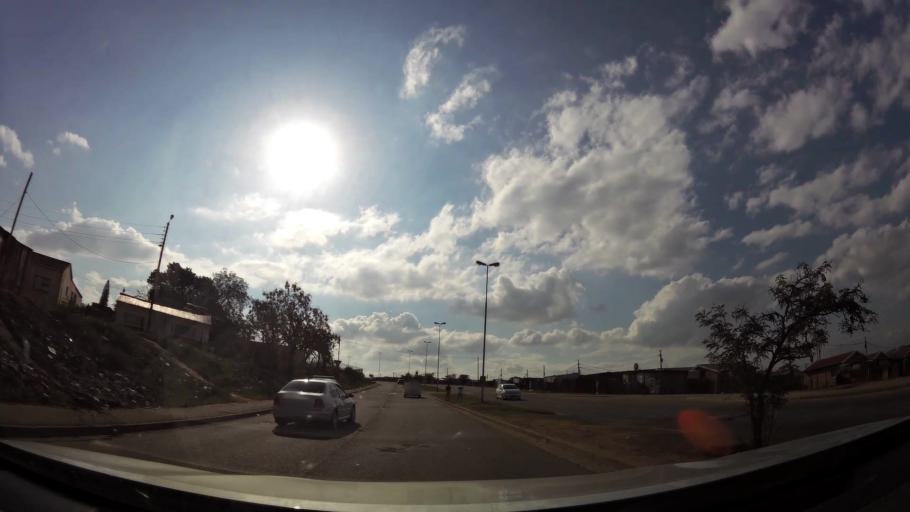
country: ZA
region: Eastern Cape
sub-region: Nelson Mandela Bay Metropolitan Municipality
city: Uitenhage
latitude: -33.7551
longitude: 25.3878
